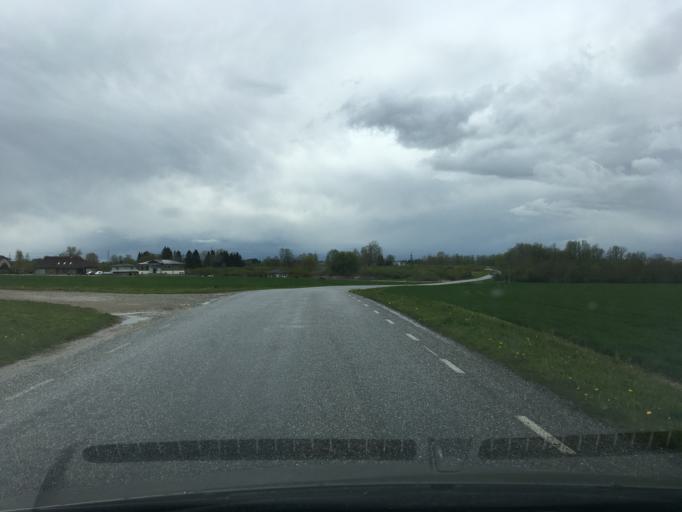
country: EE
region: Harju
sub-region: Joelaehtme vald
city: Loo
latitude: 59.4208
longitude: 24.9800
